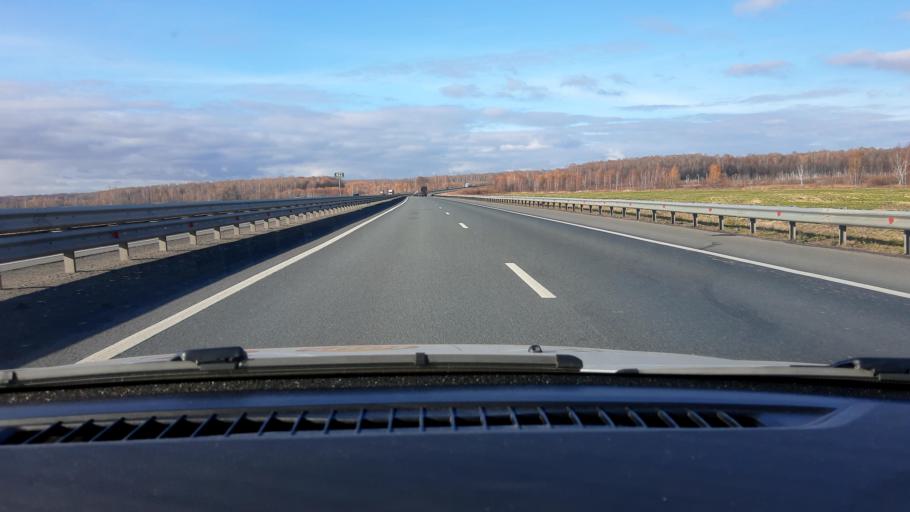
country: RU
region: Nizjnij Novgorod
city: Burevestnik
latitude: 56.1246
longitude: 43.7981
